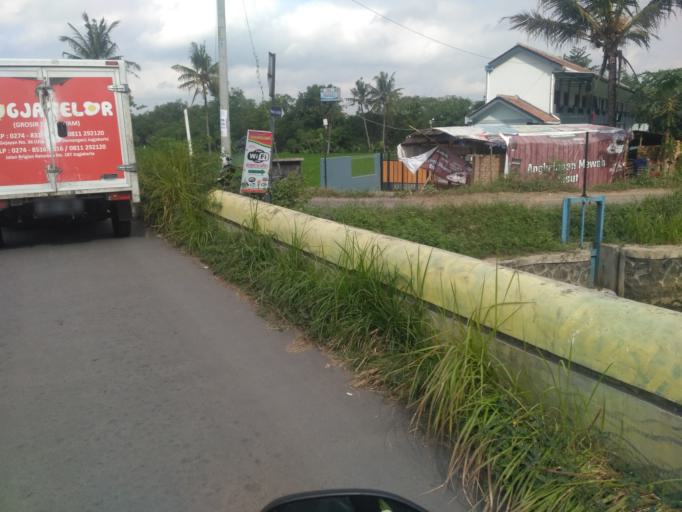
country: ID
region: Daerah Istimewa Yogyakarta
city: Melati
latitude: -7.7535
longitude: 110.3551
